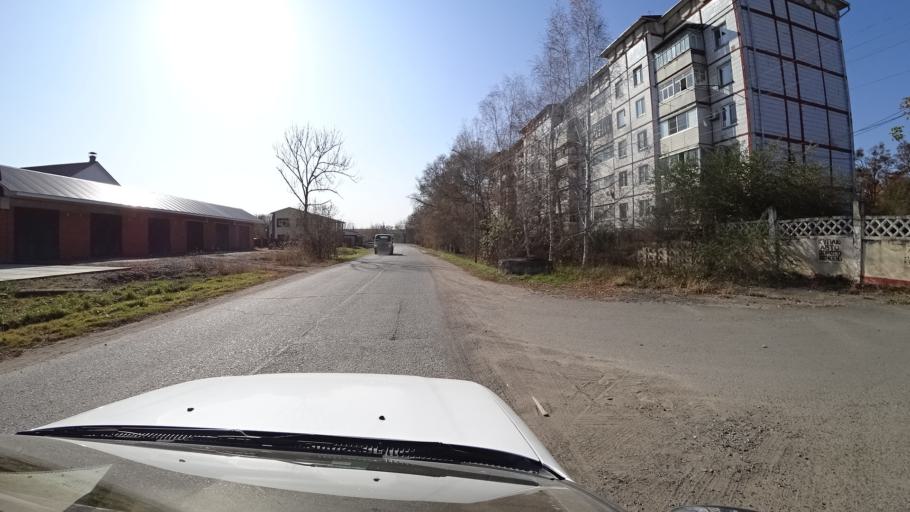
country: RU
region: Primorskiy
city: Dal'nerechensk
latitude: 45.9310
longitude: 133.7249
